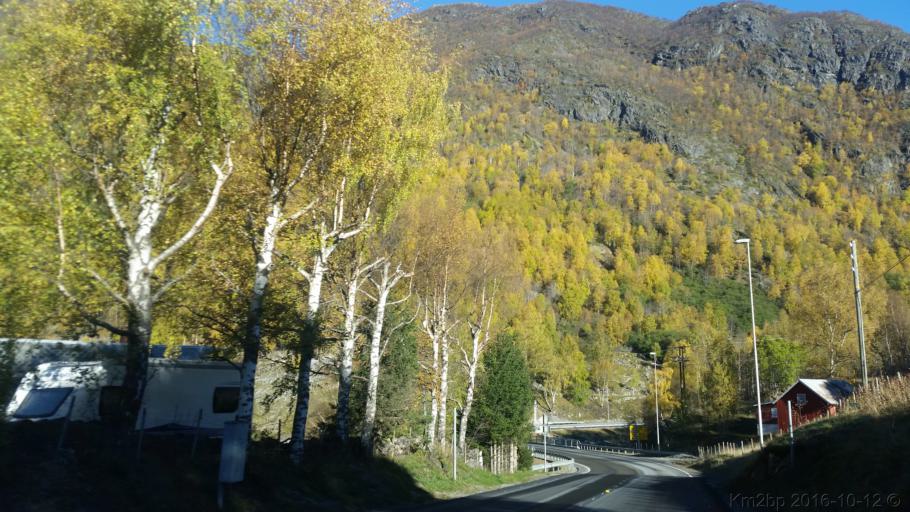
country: NO
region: Sogn og Fjordane
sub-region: Ardal
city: Farnes
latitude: 61.0717
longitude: 7.9541
